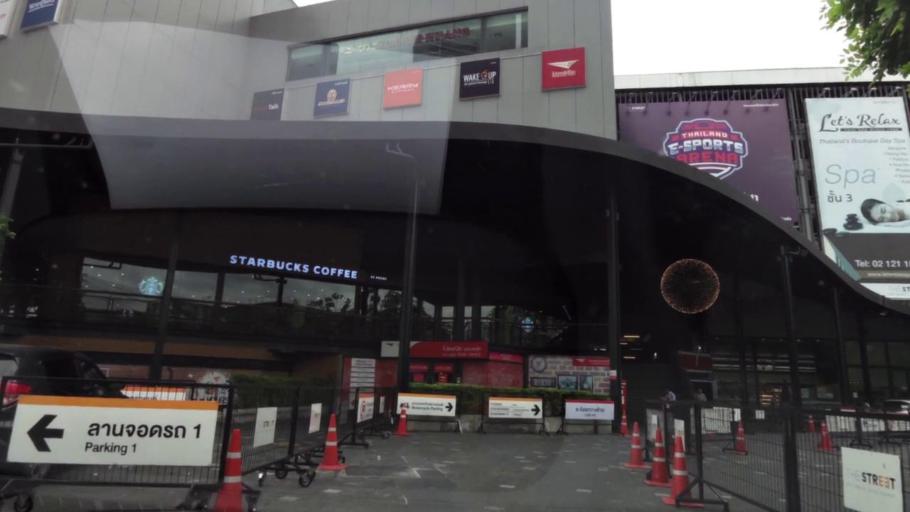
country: TH
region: Bangkok
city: Huai Khwang
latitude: 13.7706
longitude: 100.5727
